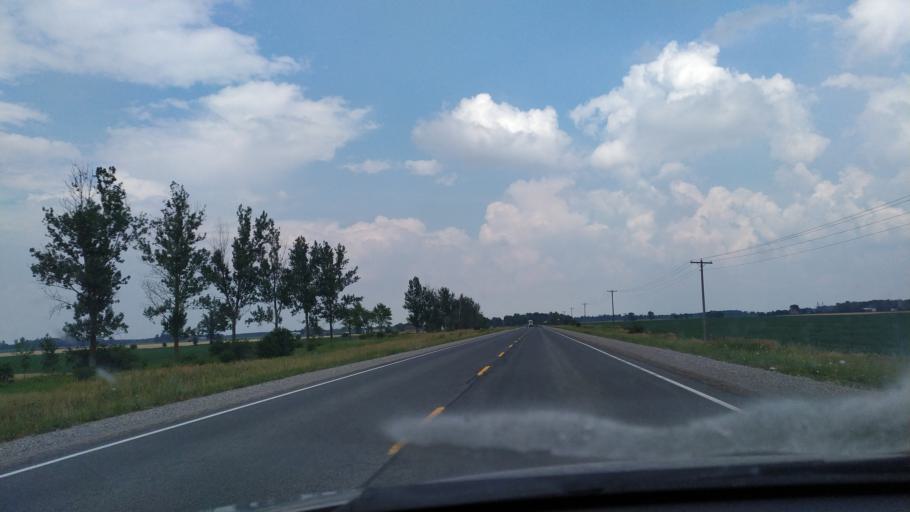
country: CA
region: Ontario
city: Stratford
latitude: 43.2417
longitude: -81.0987
